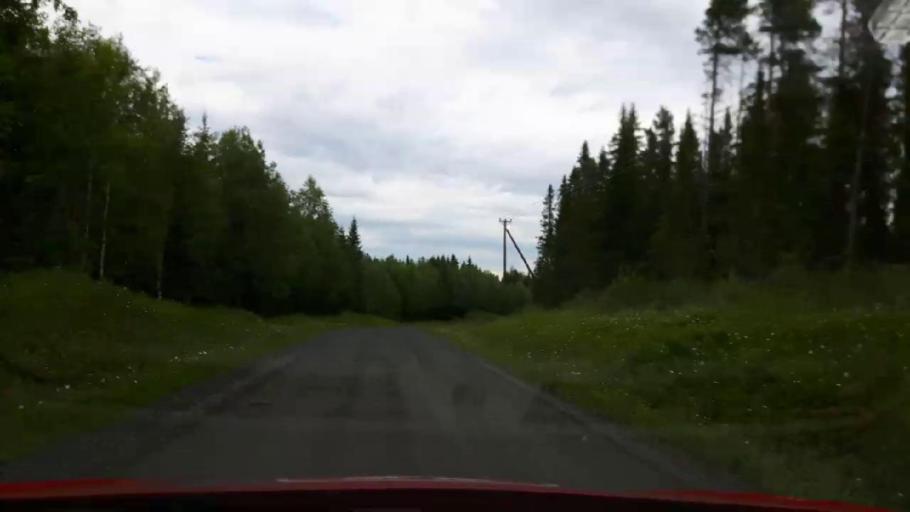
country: SE
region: Jaemtland
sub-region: Stroemsunds Kommun
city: Stroemsund
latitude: 63.4690
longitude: 15.2865
